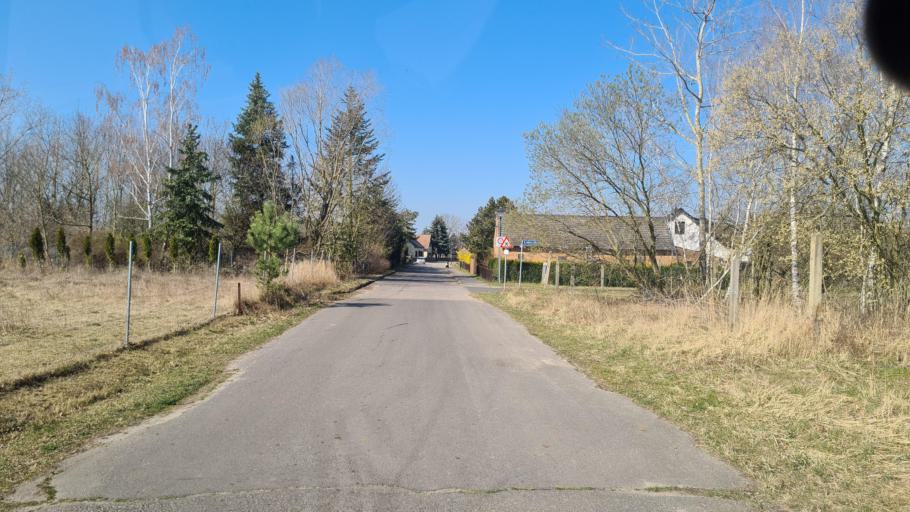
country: DE
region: Brandenburg
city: Calau
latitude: 51.7984
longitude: 13.9767
